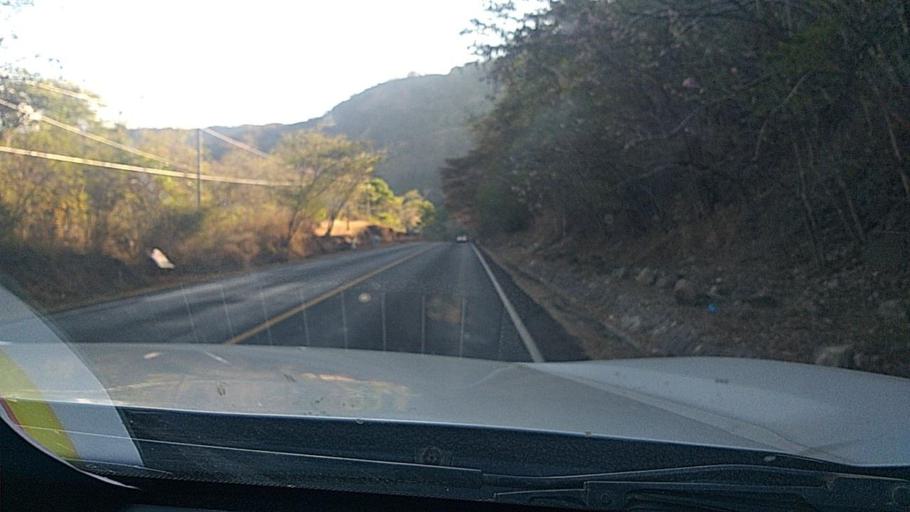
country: NI
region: Esteli
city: Condega
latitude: 13.2742
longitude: -86.3529
